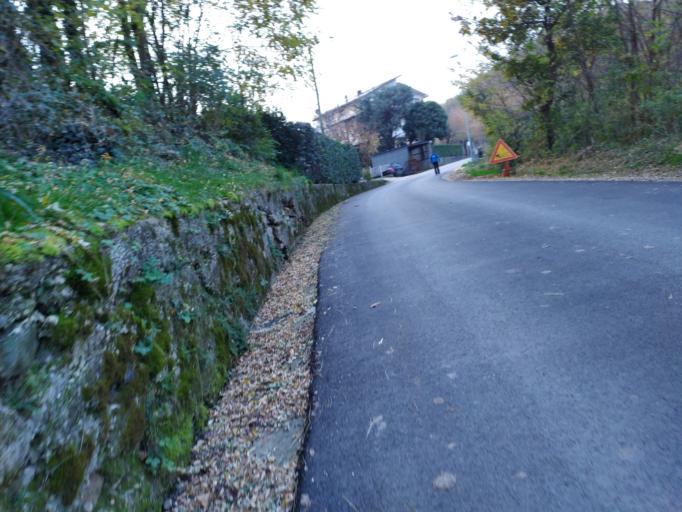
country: IT
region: Veneto
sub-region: Provincia di Vicenza
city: Schio
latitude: 45.6878
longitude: 11.3590
